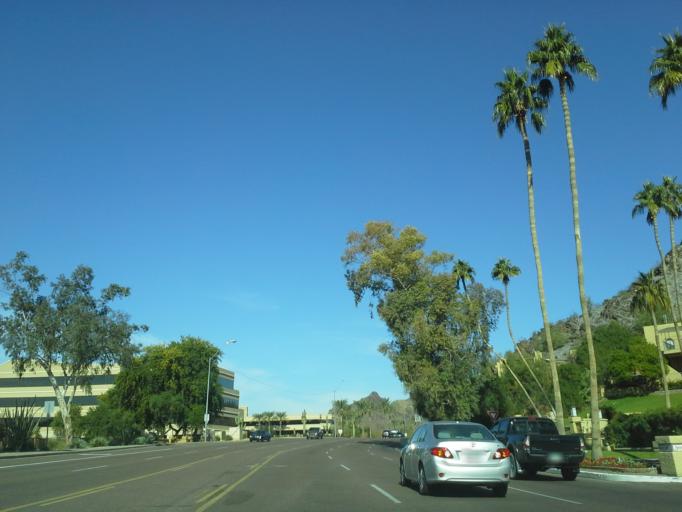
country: US
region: Arizona
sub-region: Maricopa County
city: Phoenix
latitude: 33.5486
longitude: -112.0478
